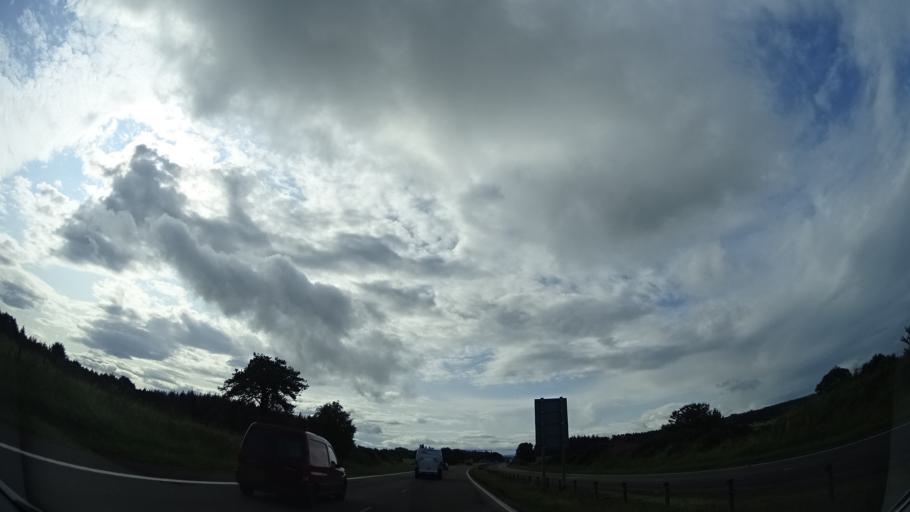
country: GB
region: Scotland
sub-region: Highland
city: Conon Bridge
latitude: 57.5369
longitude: -4.3309
